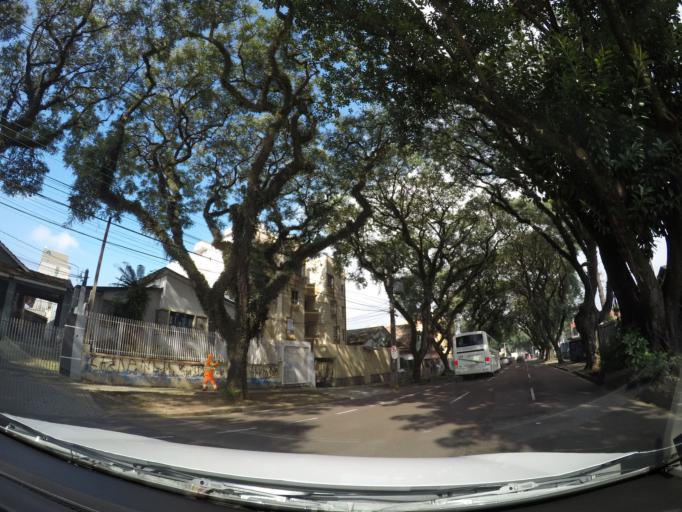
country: BR
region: Parana
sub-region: Curitiba
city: Curitiba
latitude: -25.4448
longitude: -49.2447
